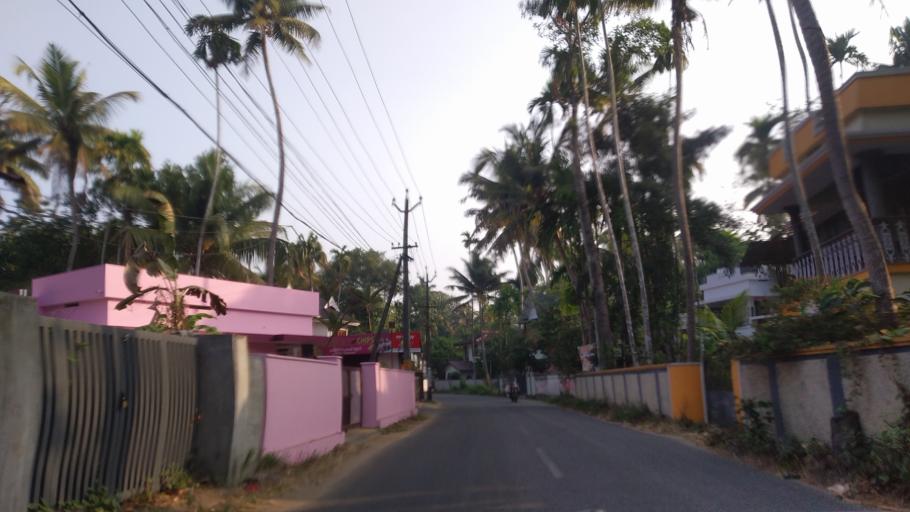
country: IN
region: Kerala
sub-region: Thrissur District
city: Kodungallur
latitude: 10.1864
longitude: 76.1980
